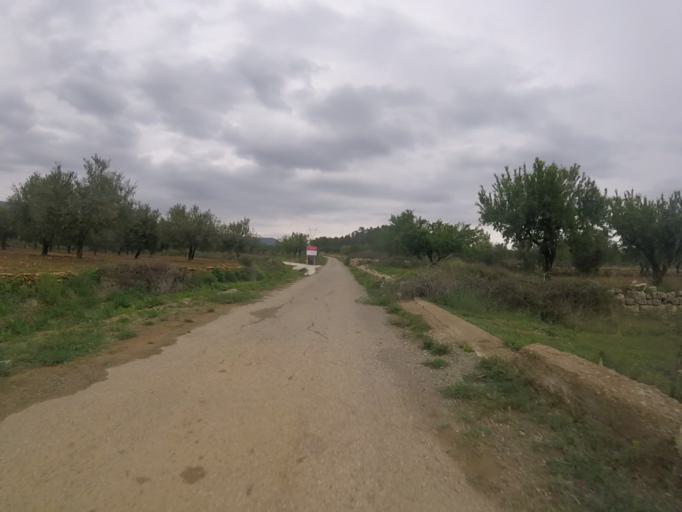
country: ES
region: Valencia
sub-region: Provincia de Castello
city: Sarratella
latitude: 40.2721
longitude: 0.0712
